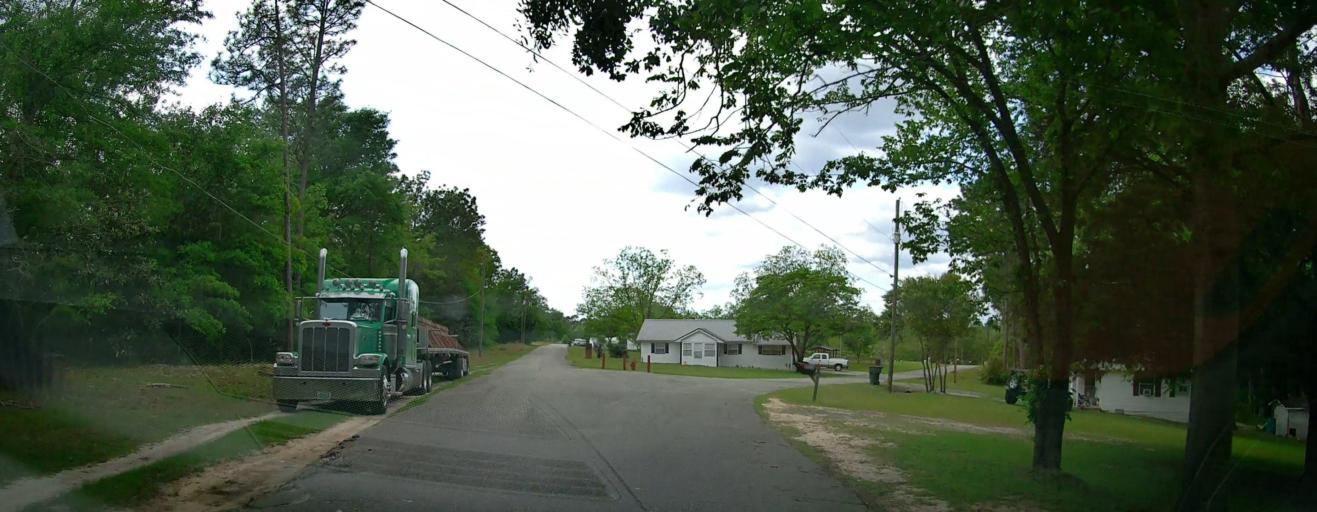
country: US
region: Georgia
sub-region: Treutlen County
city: Soperton
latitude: 32.3650
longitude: -82.5911
